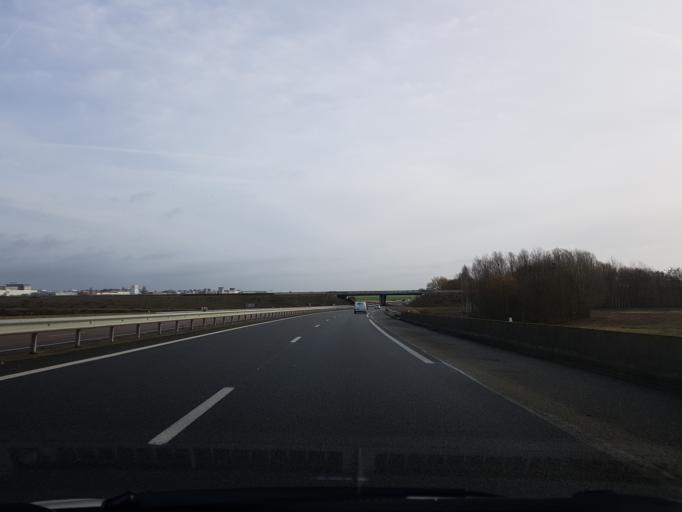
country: FR
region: Ile-de-France
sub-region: Departement de Seine-et-Marne
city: Vert-Saint-Denis
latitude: 48.5947
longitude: 2.6317
